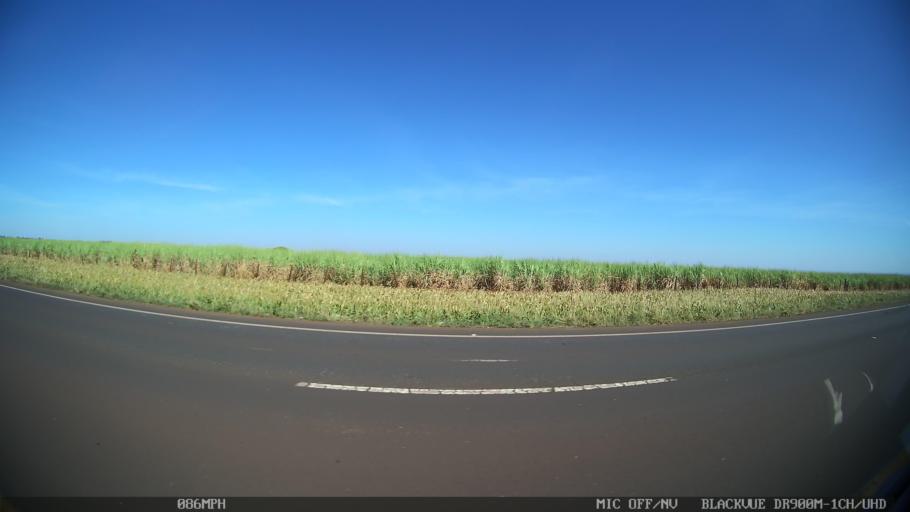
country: BR
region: Sao Paulo
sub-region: Ipua
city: Ipua
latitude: -20.4744
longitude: -48.0981
